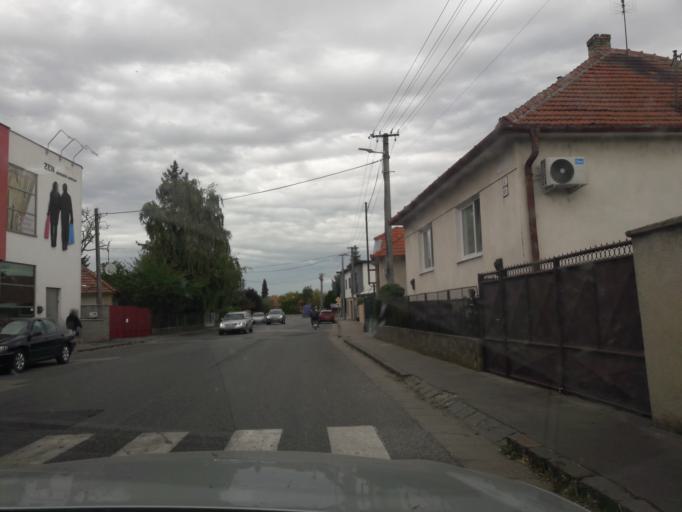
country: SK
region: Nitriansky
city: Surany
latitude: 48.0898
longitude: 18.1843
